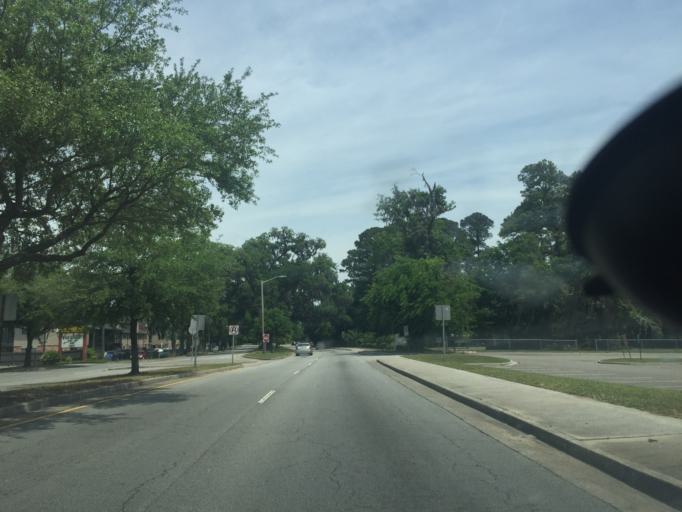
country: US
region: Georgia
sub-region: Chatham County
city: Montgomery
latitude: 31.9917
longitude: -81.1276
